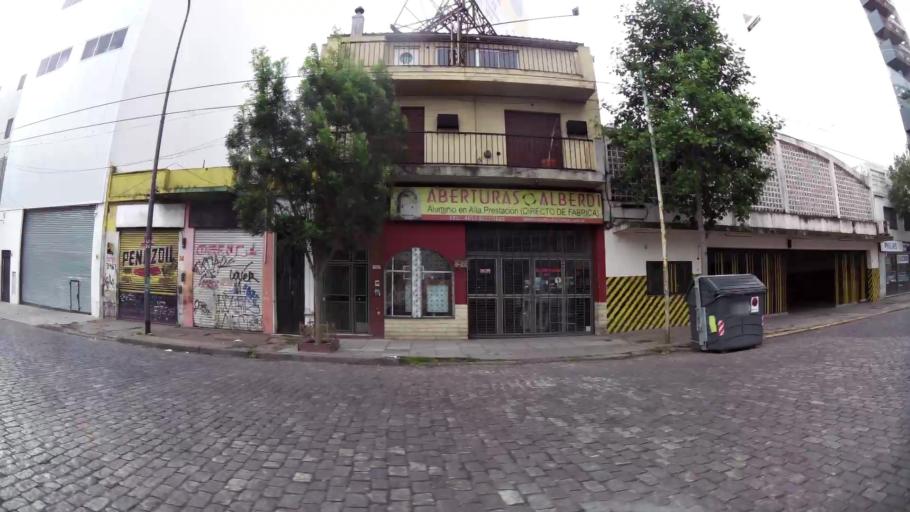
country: AR
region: Buenos Aires F.D.
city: Villa Santa Rita
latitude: -34.6354
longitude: -58.4750
